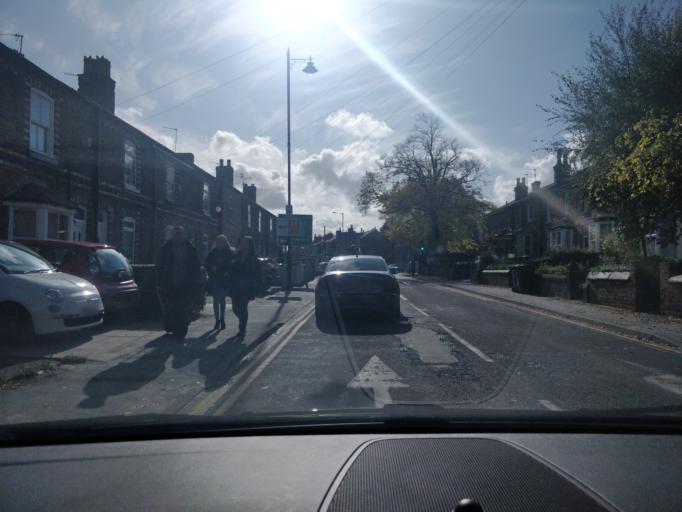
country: GB
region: England
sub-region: Lancashire
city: Ormskirk
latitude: 53.5674
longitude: -2.8814
